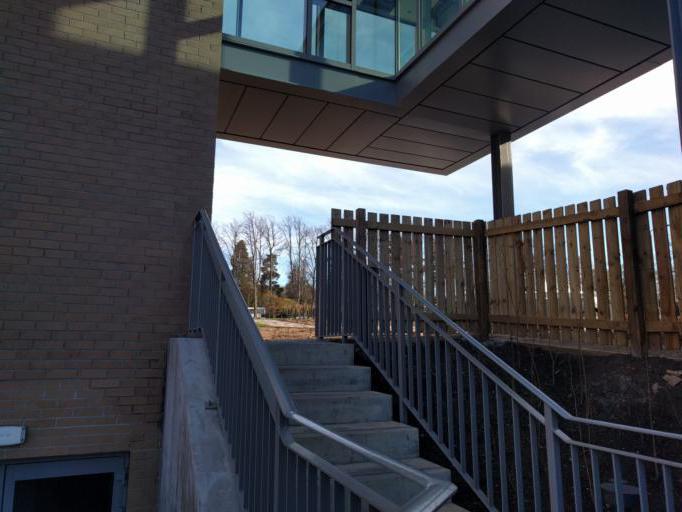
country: GB
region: Scotland
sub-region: Edinburgh
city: Currie
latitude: 55.9124
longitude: -3.3157
